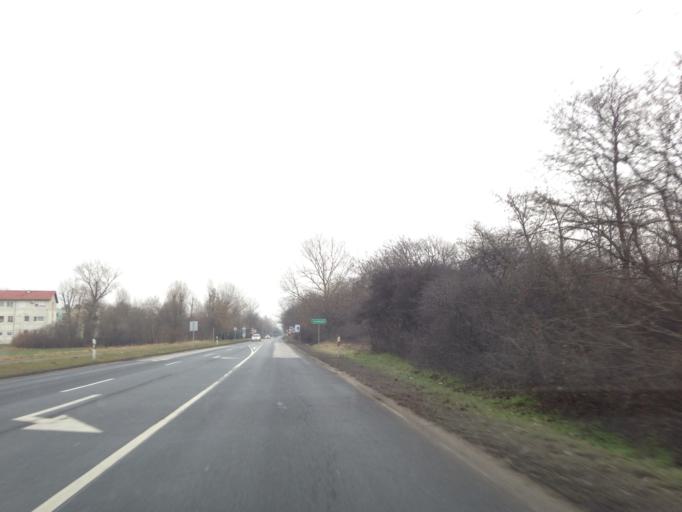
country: HU
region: Komarom-Esztergom
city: Almasfuzito
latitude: 47.7326
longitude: 18.2117
